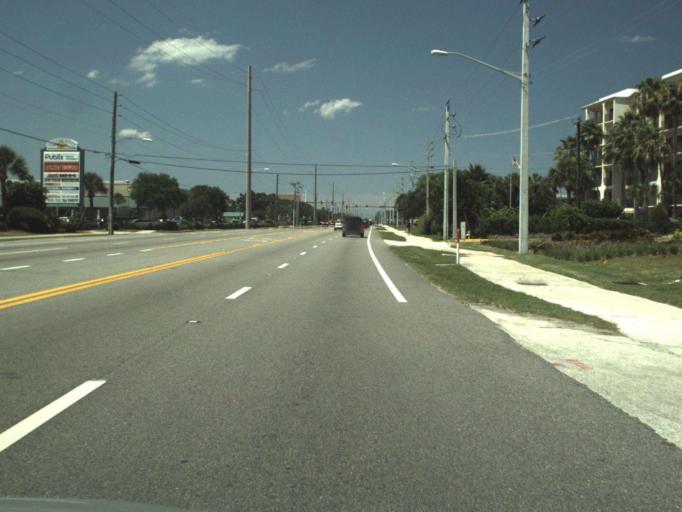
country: US
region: Florida
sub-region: Brevard County
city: Cocoa Beach
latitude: 28.3429
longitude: -80.6099
